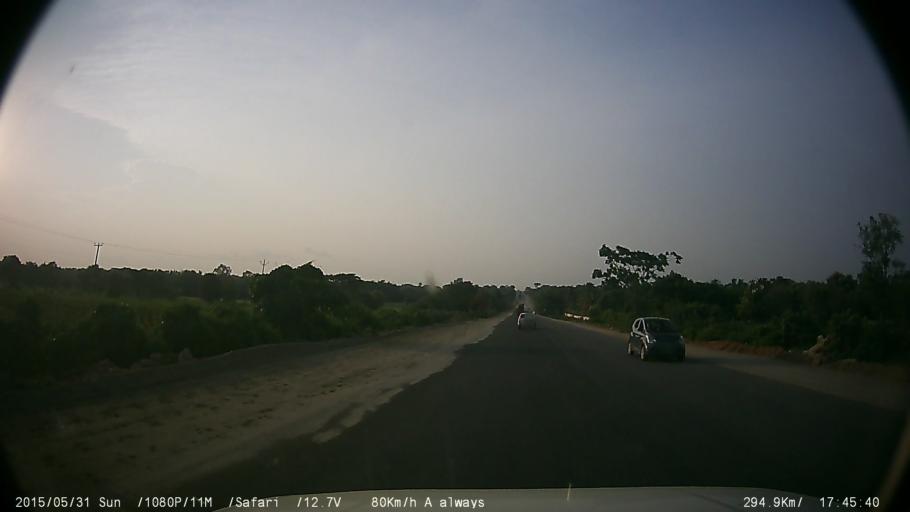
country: IN
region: Karnataka
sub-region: Chamrajnagar
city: Gundlupet
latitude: 11.9521
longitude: 76.6707
